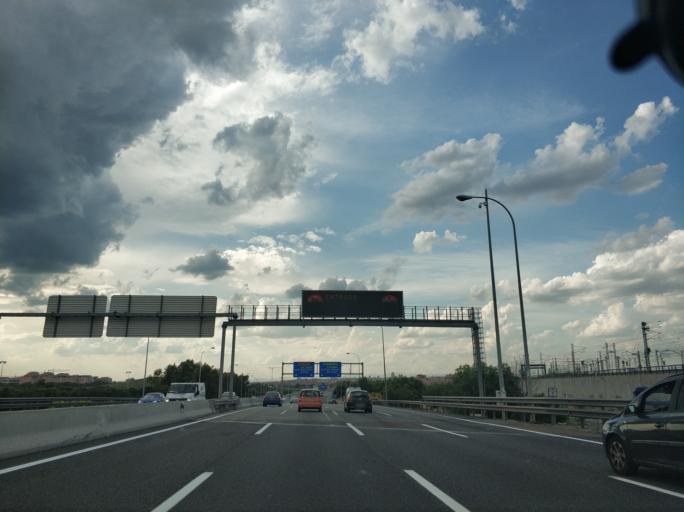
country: ES
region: Madrid
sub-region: Provincia de Madrid
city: Usera
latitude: 40.3744
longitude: -3.6819
